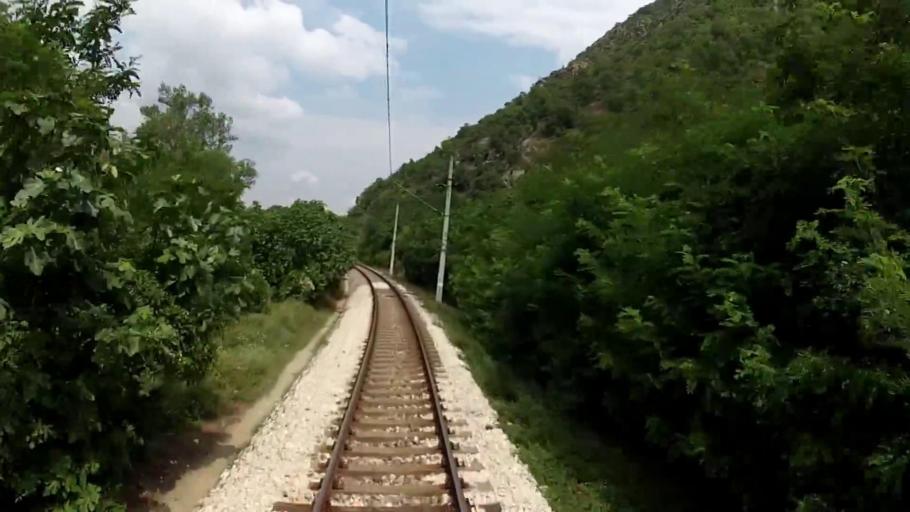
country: BG
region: Blagoevgrad
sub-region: Obshtina Kresna
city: Stara Kresna
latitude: 41.8335
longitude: 23.1557
